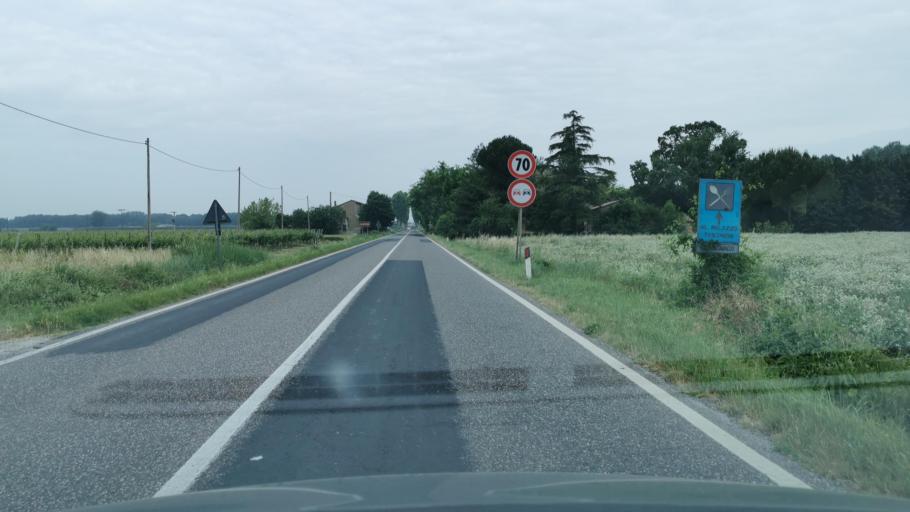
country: IT
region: Emilia-Romagna
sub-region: Provincia di Ravenna
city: Russi
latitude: 44.3974
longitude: 12.0337
